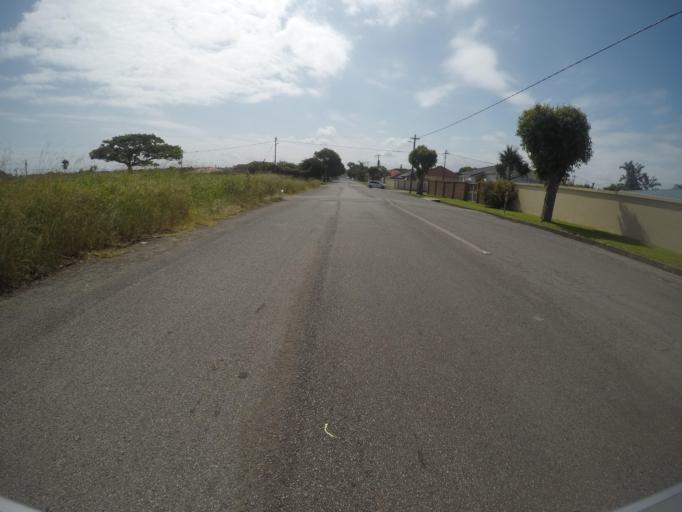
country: ZA
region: Eastern Cape
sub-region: Buffalo City Metropolitan Municipality
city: East London
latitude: -32.9782
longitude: 27.8725
